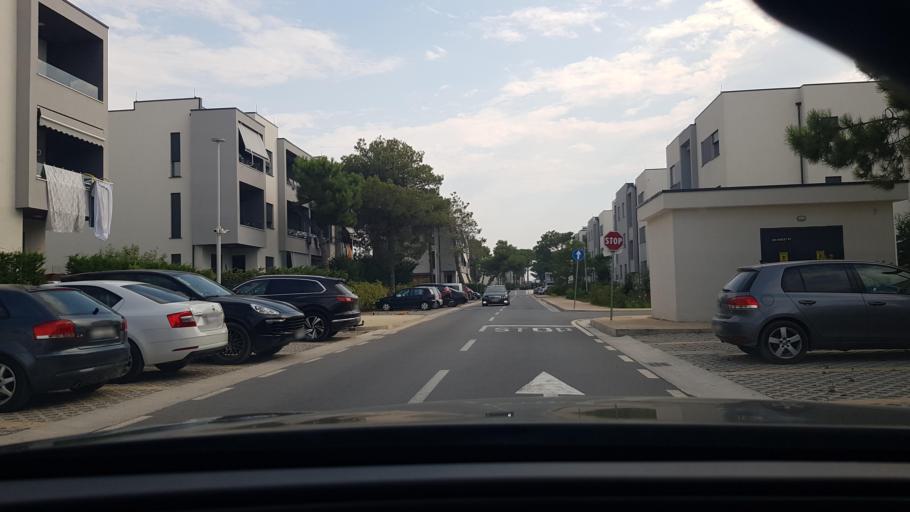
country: AL
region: Durres
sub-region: Rrethi i Durresit
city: Katundi i Ri
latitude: 41.4901
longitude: 19.5131
